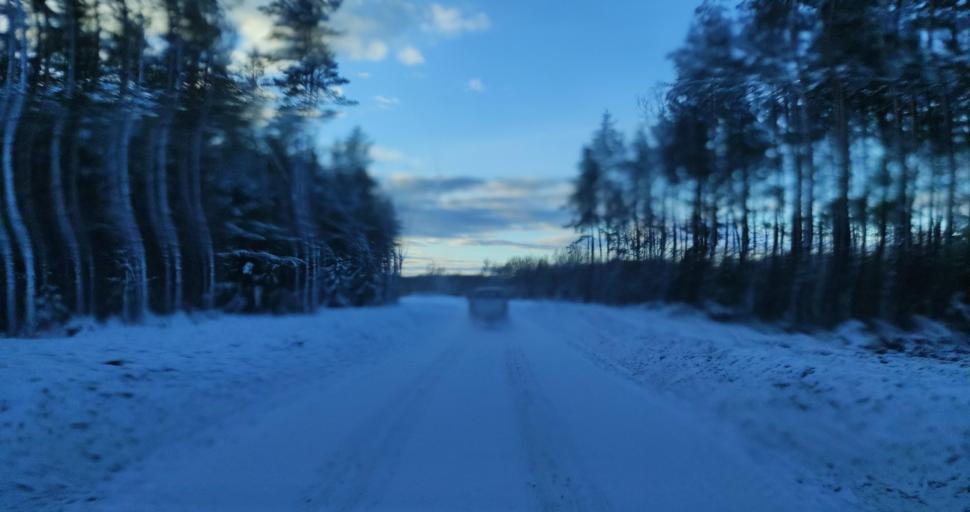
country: LV
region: Skrunda
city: Skrunda
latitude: 56.5893
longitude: 21.9524
